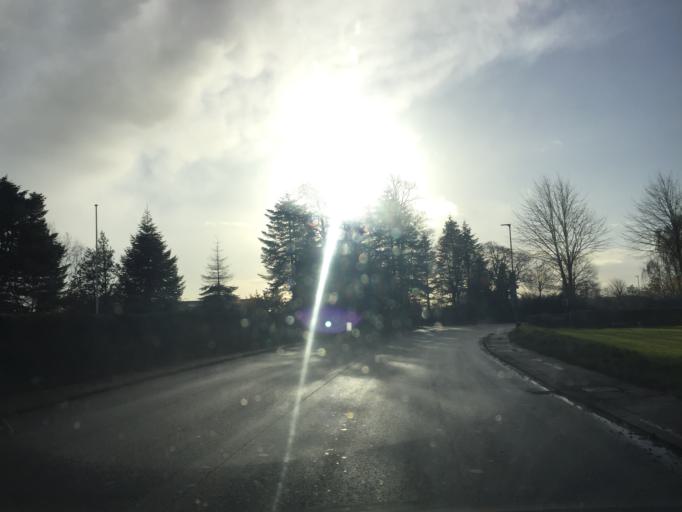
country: DK
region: South Denmark
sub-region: Kolding Kommune
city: Sonder Bjert
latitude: 55.4613
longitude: 9.6182
